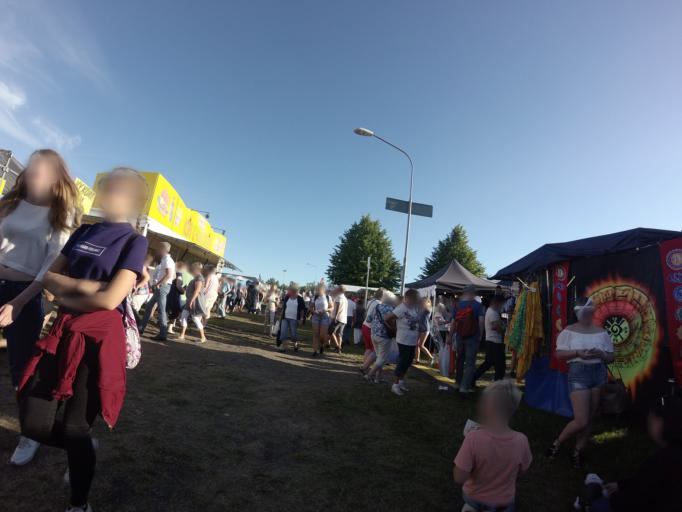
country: SE
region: Skane
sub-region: Sjobo Kommun
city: Sjoebo
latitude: 55.6311
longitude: 13.7109
